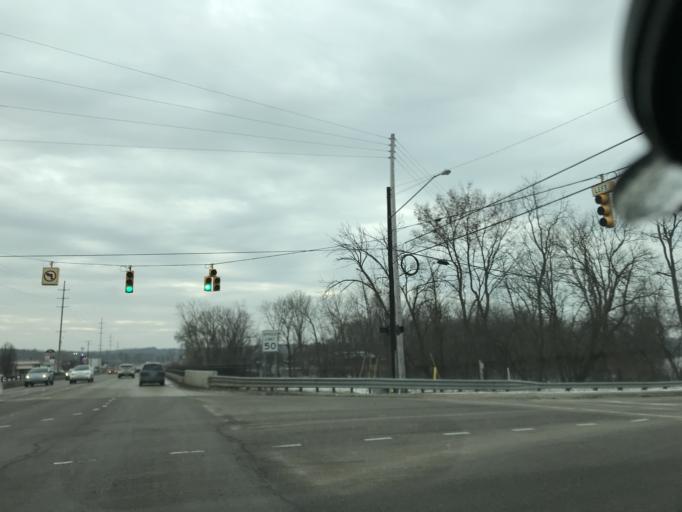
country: US
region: Michigan
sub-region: Kent County
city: Northview
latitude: 43.0646
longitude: -85.5800
